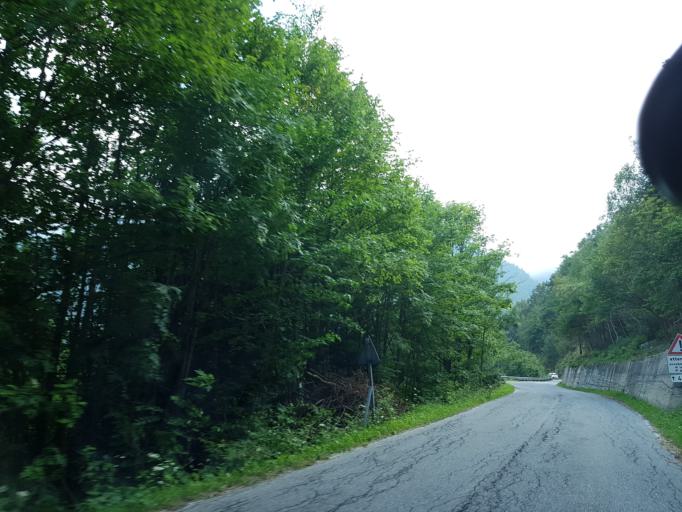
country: IT
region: Piedmont
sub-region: Provincia di Cuneo
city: Casteldelfino
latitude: 44.5923
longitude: 7.0661
